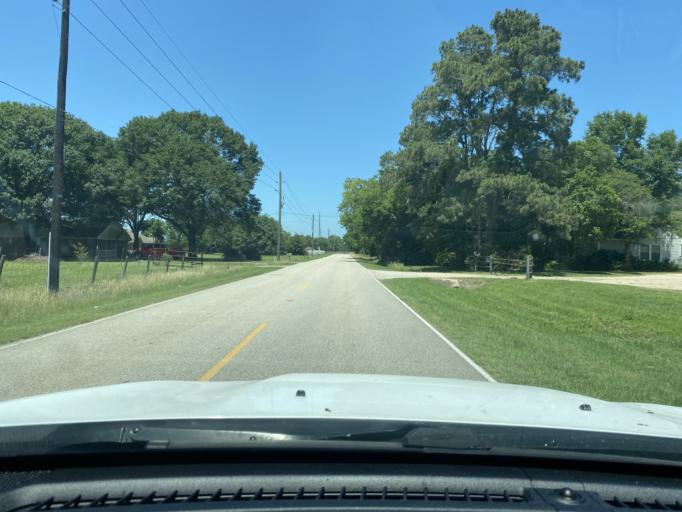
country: US
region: Texas
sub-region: Waller County
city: Waller
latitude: 30.0145
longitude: -95.8487
